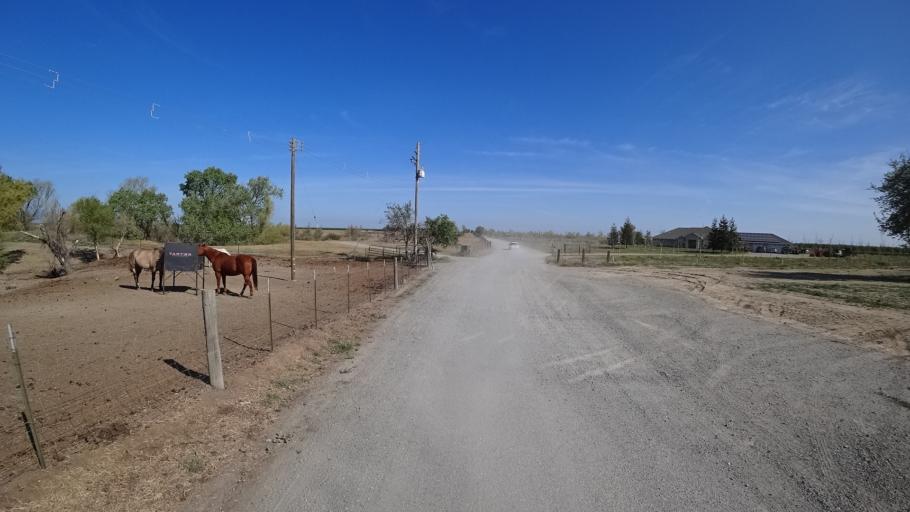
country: US
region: California
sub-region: Glenn County
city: Willows
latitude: 39.5566
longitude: -122.1558
